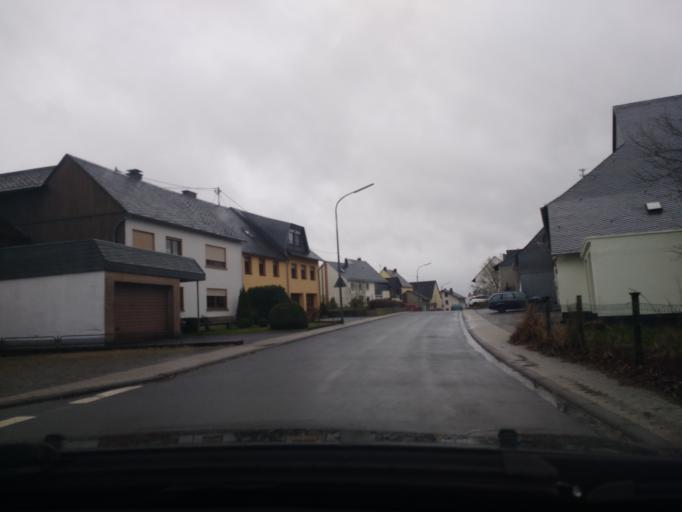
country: DE
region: Rheinland-Pfalz
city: Irmenach
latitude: 49.9266
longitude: 7.1903
